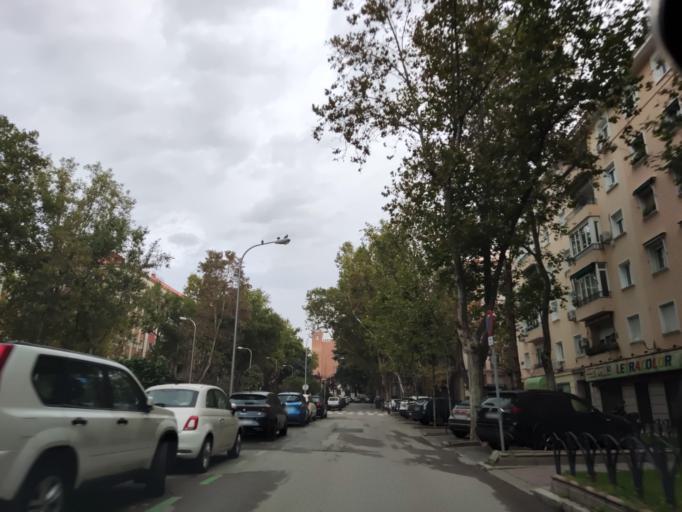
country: ES
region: Madrid
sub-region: Provincia de Madrid
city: Chamberi
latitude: 40.4535
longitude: -3.6972
